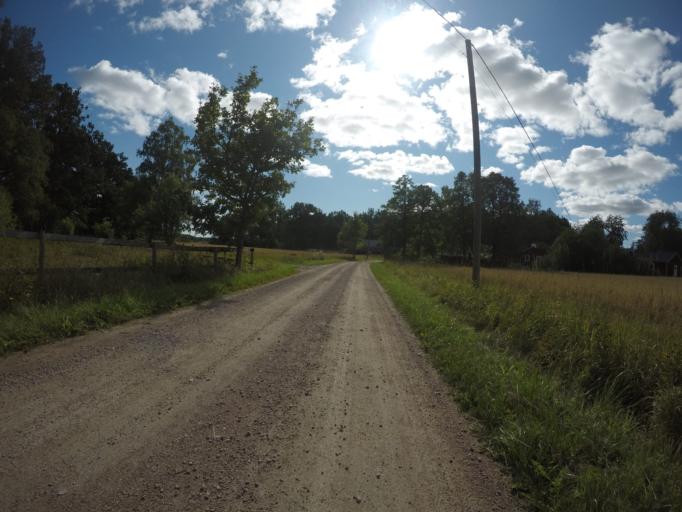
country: SE
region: Vaestmanland
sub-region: Hallstahammars Kommun
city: Kolback
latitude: 59.4949
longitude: 16.2123
